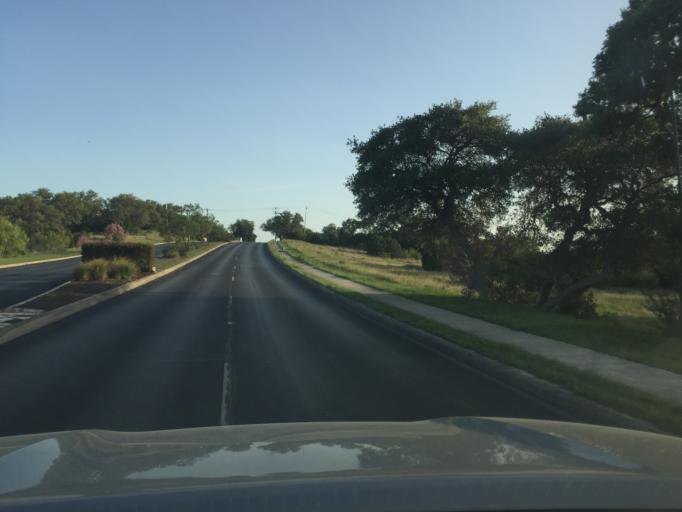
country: US
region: Texas
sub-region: Bexar County
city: Timberwood Park
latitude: 29.6614
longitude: -98.4789
